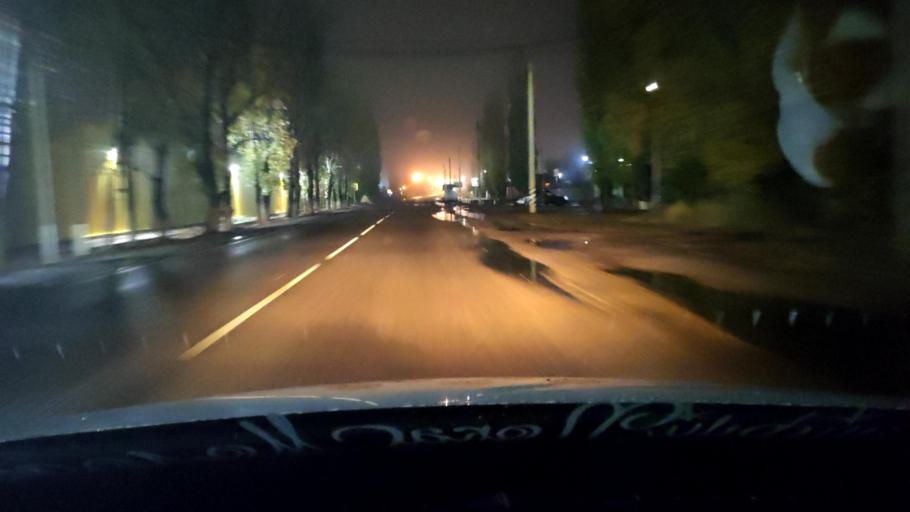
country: RU
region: Voronezj
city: Semiluki
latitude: 51.6916
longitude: 38.9959
